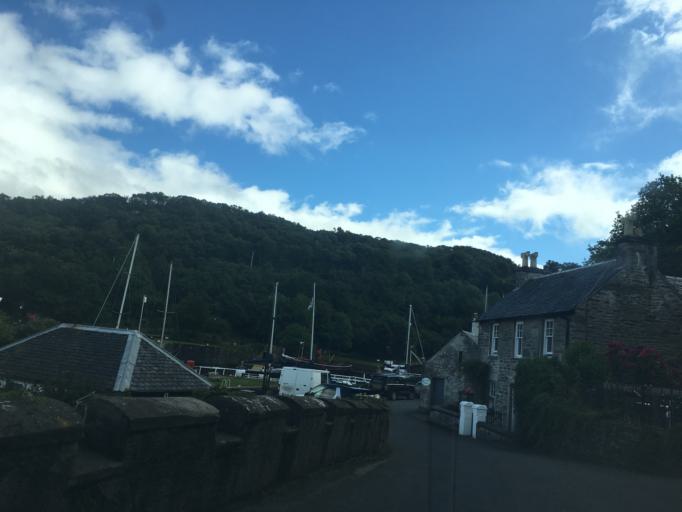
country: GB
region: Scotland
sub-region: Argyll and Bute
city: Ardrishaig
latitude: 56.0914
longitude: -5.5570
